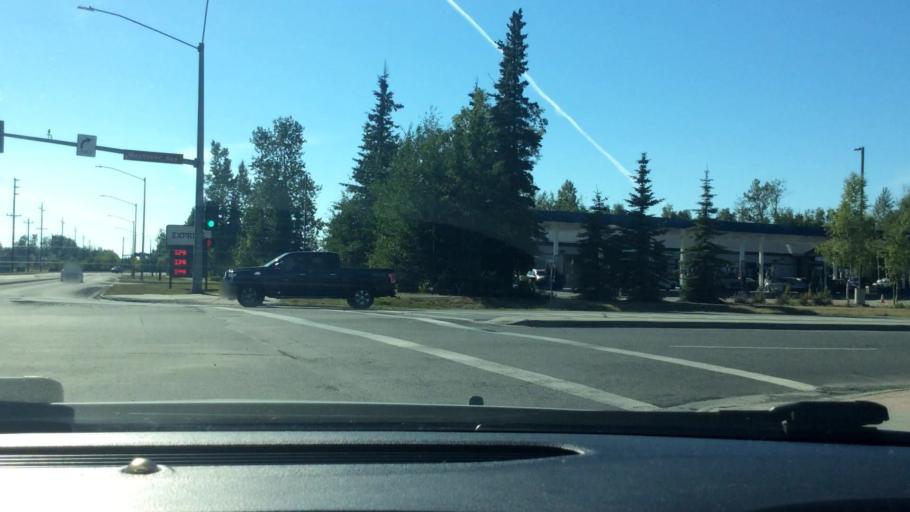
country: US
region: Alaska
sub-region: Anchorage Municipality
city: Elmendorf Air Force Base
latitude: 61.2315
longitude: -149.7614
